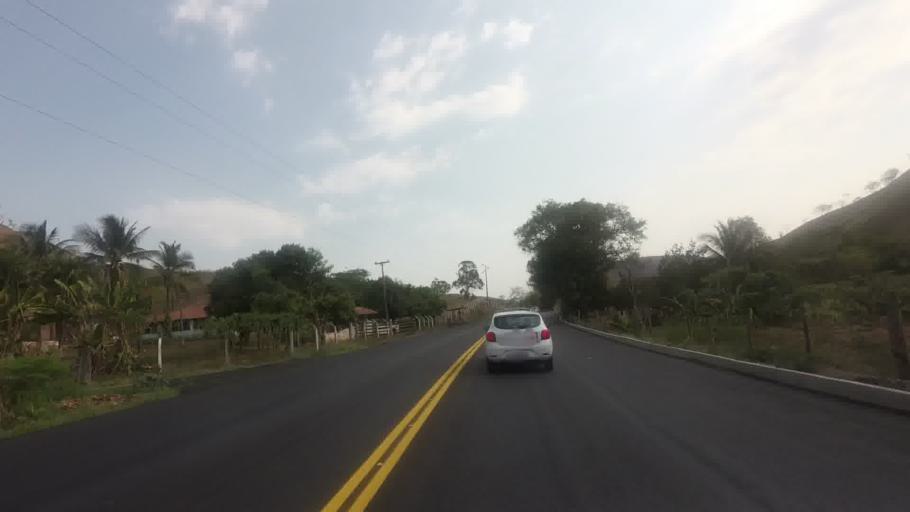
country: BR
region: Rio de Janeiro
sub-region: Bom Jesus Do Itabapoana
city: Bom Jesus do Itabapoana
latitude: -21.2211
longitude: -41.7391
